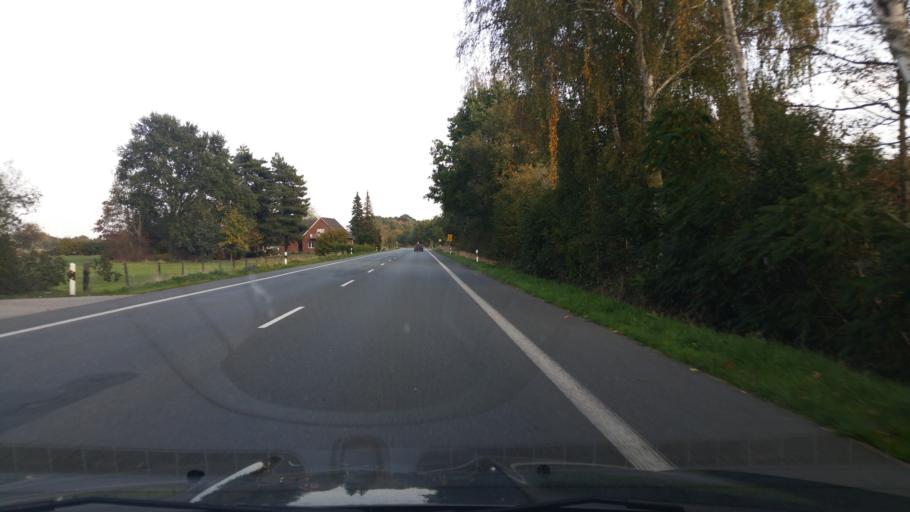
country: DE
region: North Rhine-Westphalia
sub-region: Regierungsbezirk Munster
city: Isselburg
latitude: 51.8615
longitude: 6.5275
